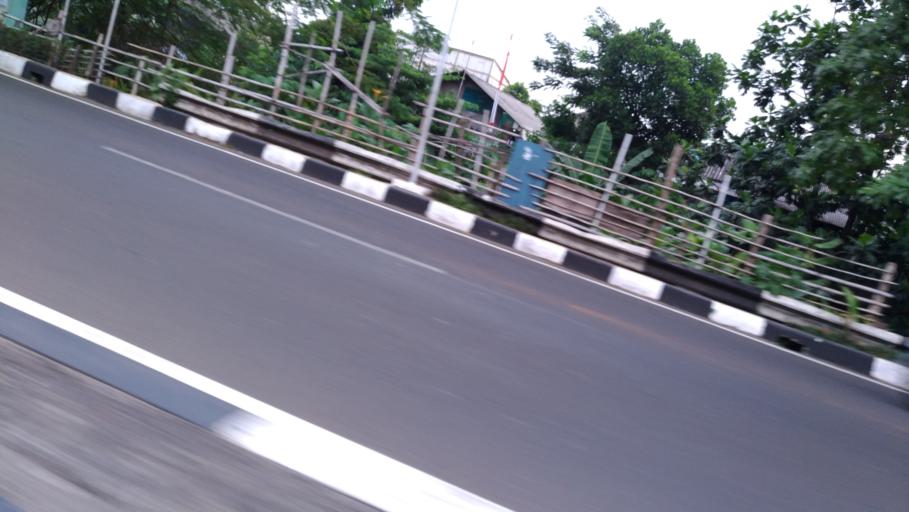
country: ID
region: West Java
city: Depok
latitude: -6.3303
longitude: 106.8667
